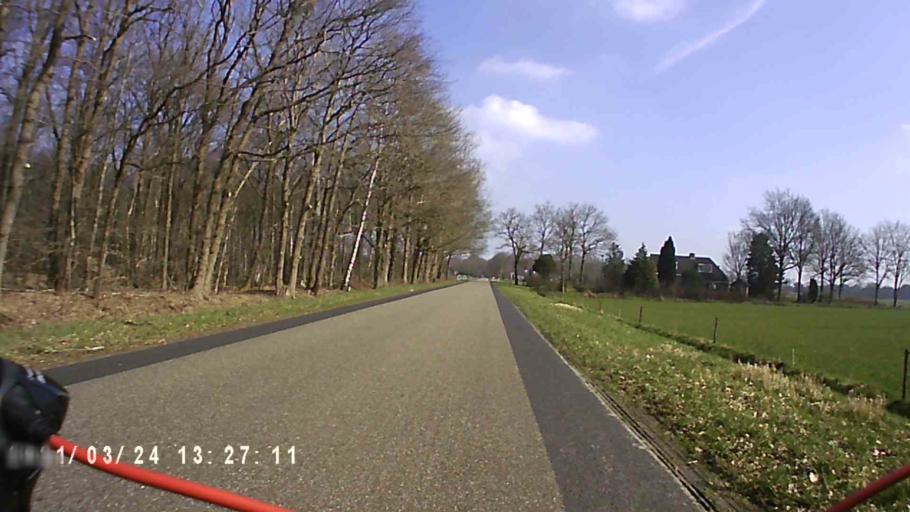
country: NL
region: Groningen
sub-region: Gemeente Leek
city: Leek
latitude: 53.0918
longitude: 6.2834
